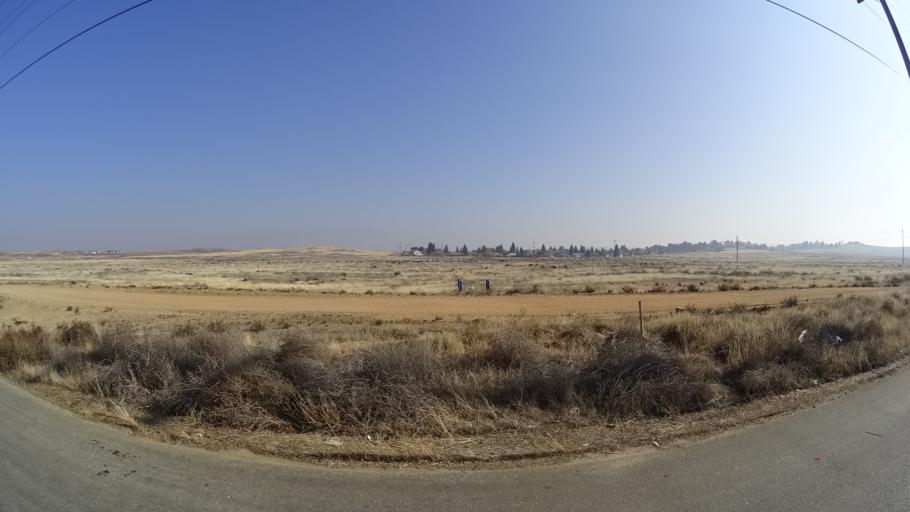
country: US
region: California
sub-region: Kern County
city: Oildale
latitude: 35.4084
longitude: -118.8788
